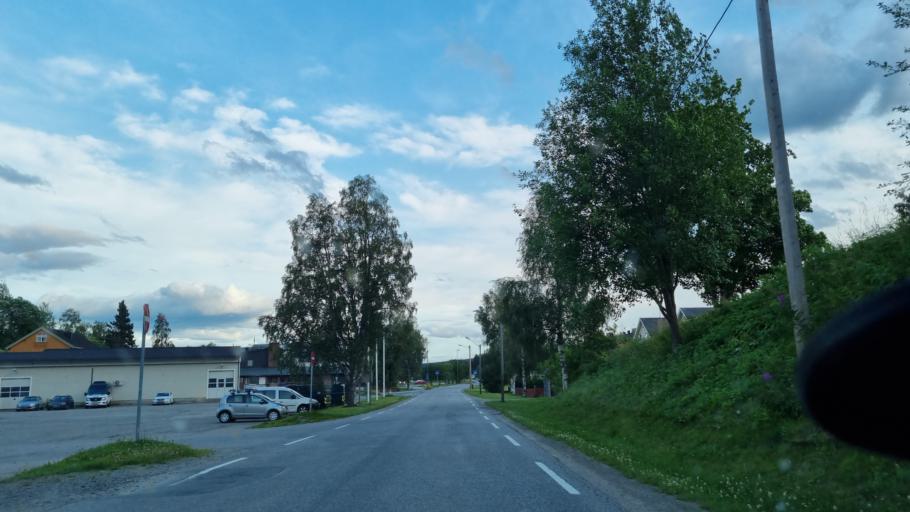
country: NO
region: Hedmark
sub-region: Trysil
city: Innbygda
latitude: 61.3190
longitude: 12.2599
